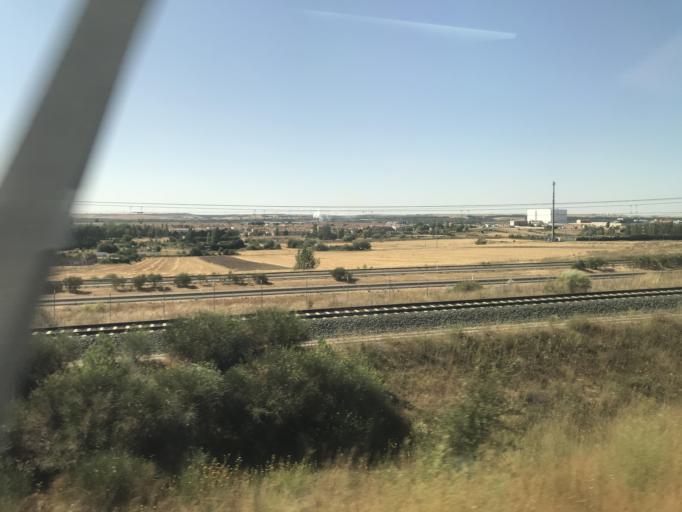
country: ES
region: Castille and Leon
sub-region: Provincia de Burgos
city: Hurones
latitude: 42.3745
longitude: -3.6145
